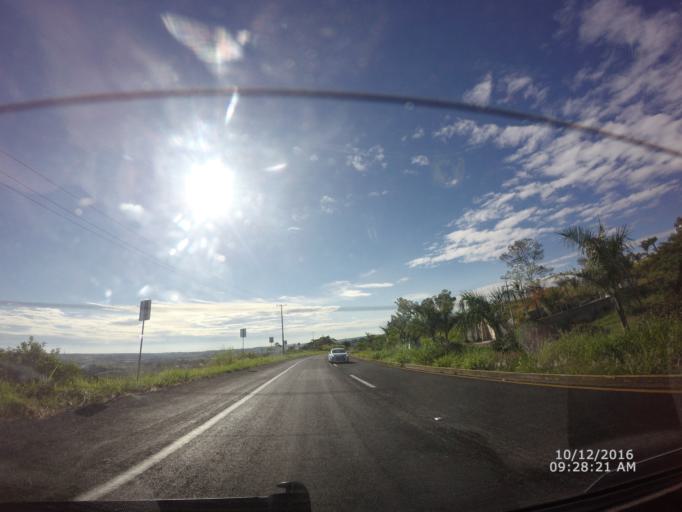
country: MX
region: Veracruz
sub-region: Emiliano Zapata
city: Dos Rios
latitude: 19.4993
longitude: -96.8224
